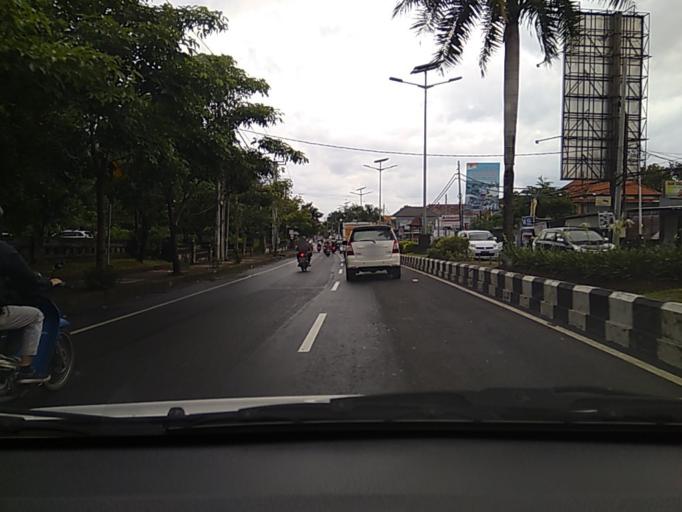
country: ID
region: Bali
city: Bualu
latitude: -8.7849
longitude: 115.1965
